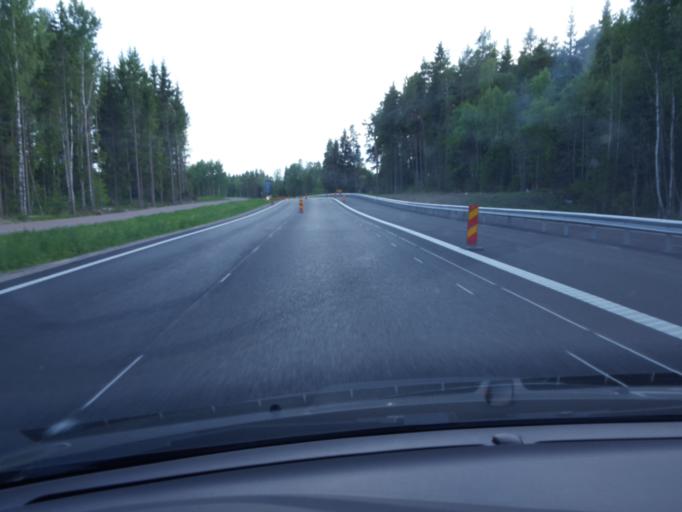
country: SE
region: Uppsala
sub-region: Osthammars Kommun
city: Gimo
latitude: 60.1093
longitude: 18.1272
